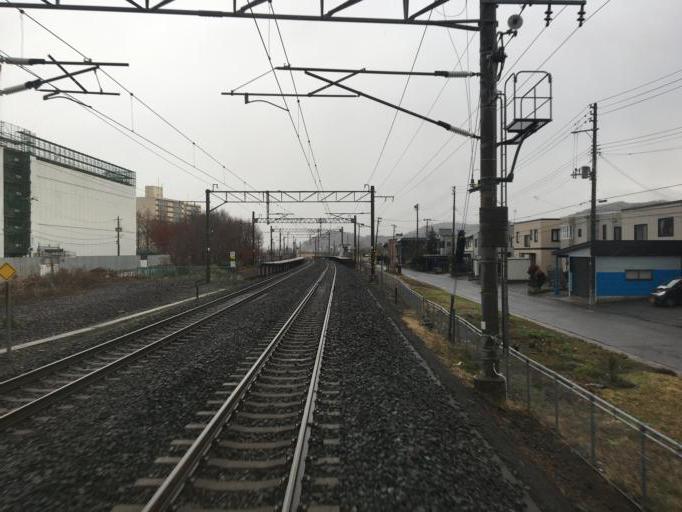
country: JP
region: Aomori
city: Aomori Shi
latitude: 40.8174
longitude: 140.7966
